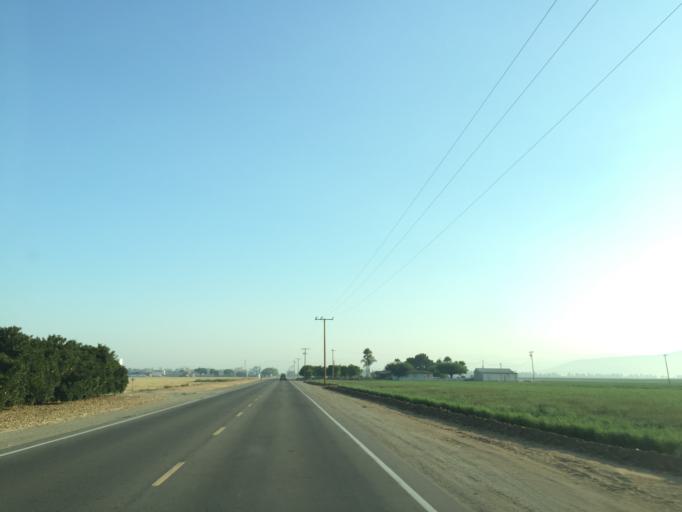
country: US
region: California
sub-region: Tulare County
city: Cutler
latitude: 36.4466
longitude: -119.2777
